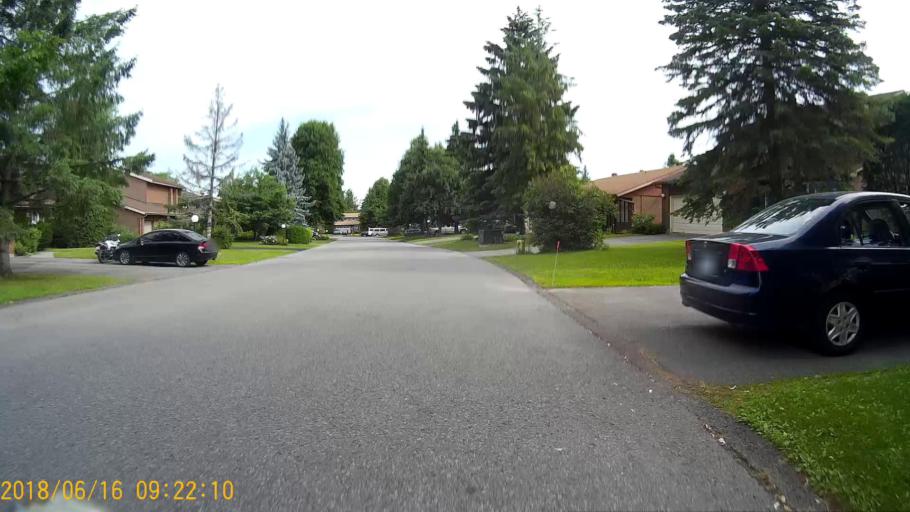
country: CA
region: Ontario
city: Bells Corners
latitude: 45.3131
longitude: -75.8897
